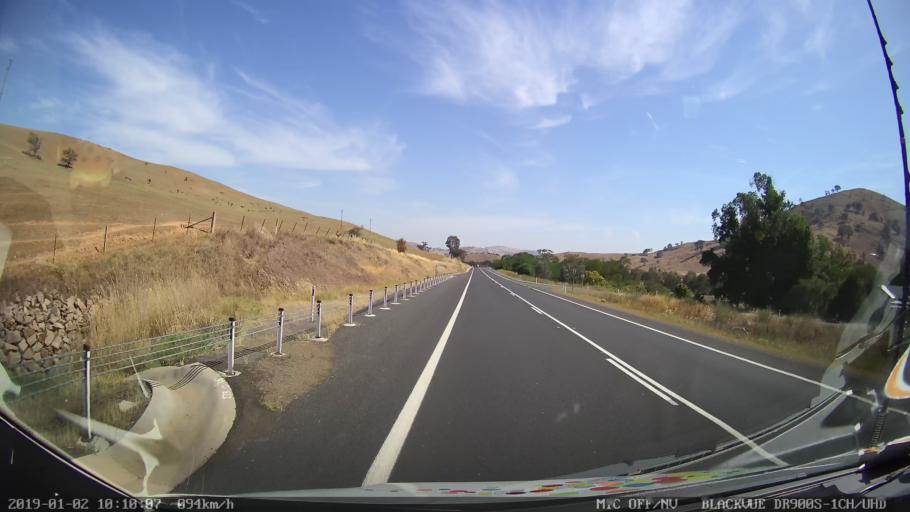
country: AU
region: New South Wales
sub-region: Gundagai
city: Gundagai
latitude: -35.1083
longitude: 148.0970
